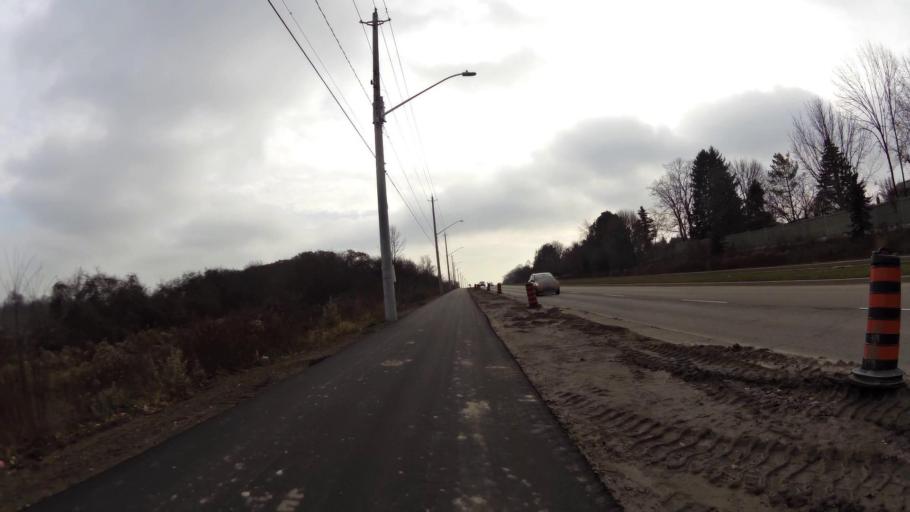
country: CA
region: Ontario
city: Kitchener
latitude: 43.4142
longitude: -80.4655
